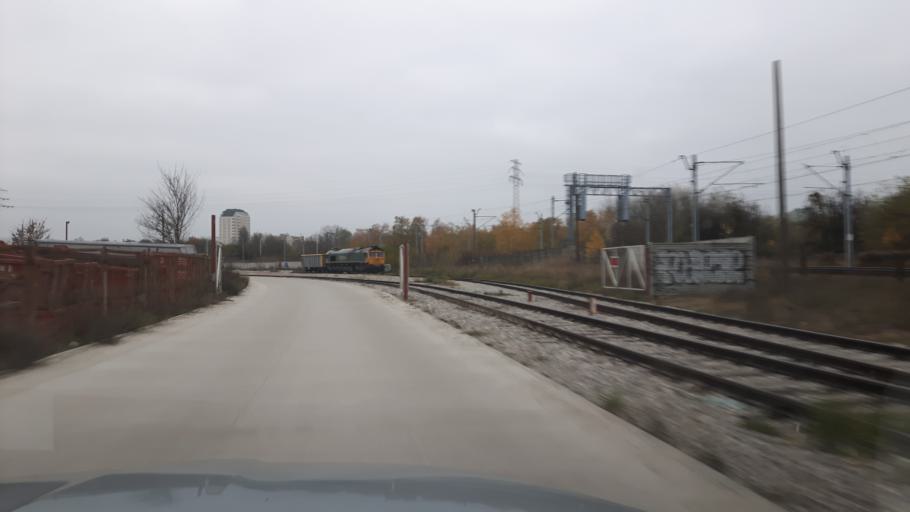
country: PL
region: Masovian Voivodeship
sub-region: Warszawa
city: Praga Polnoc
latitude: 52.2699
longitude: 21.0285
